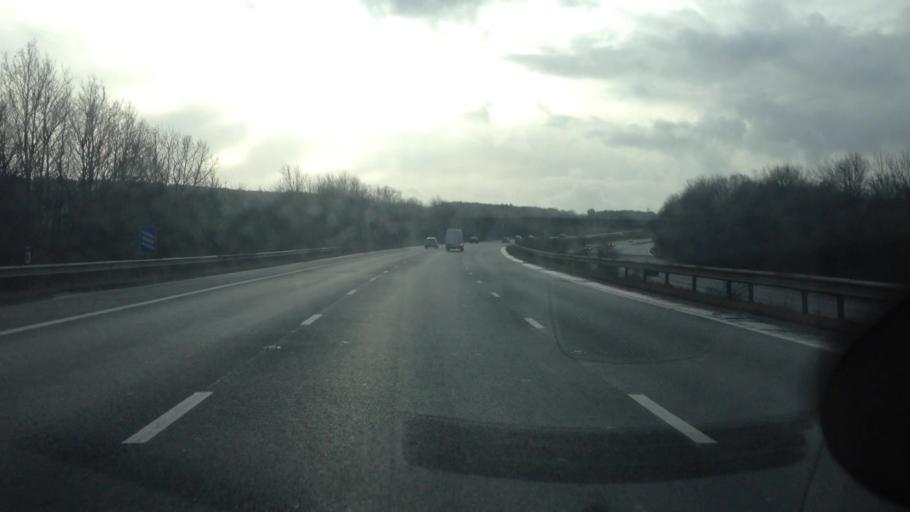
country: GB
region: England
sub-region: City and Borough of Wakefield
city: Crigglestone
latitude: 53.6319
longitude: -1.5399
